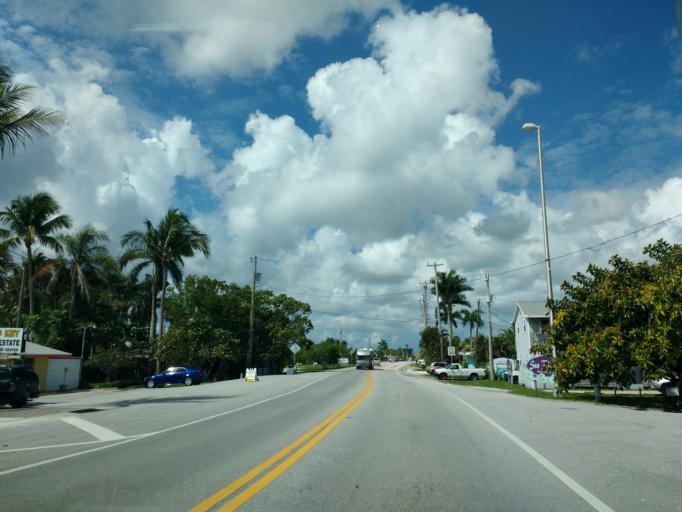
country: US
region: Florida
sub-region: Lee County
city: Pine Island Center
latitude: 26.6318
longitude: -82.0687
